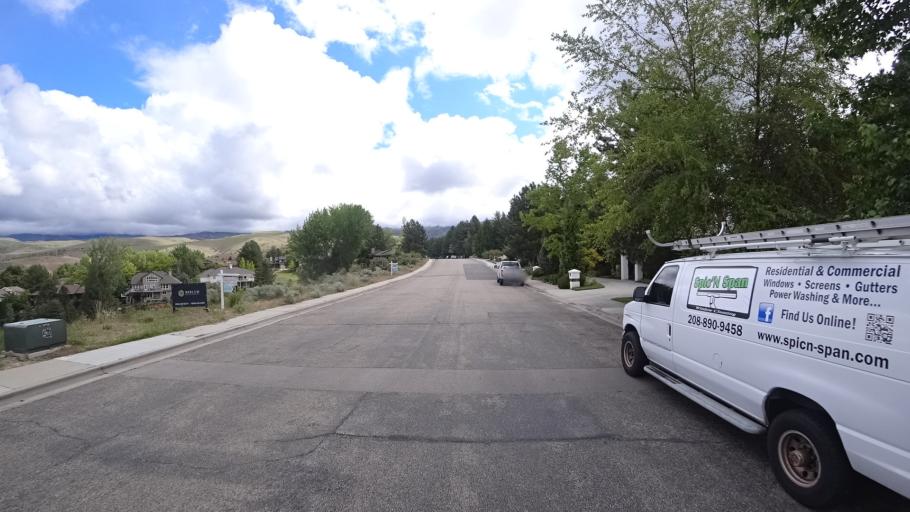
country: US
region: Idaho
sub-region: Ada County
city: Boise
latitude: 43.6526
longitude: -116.1774
